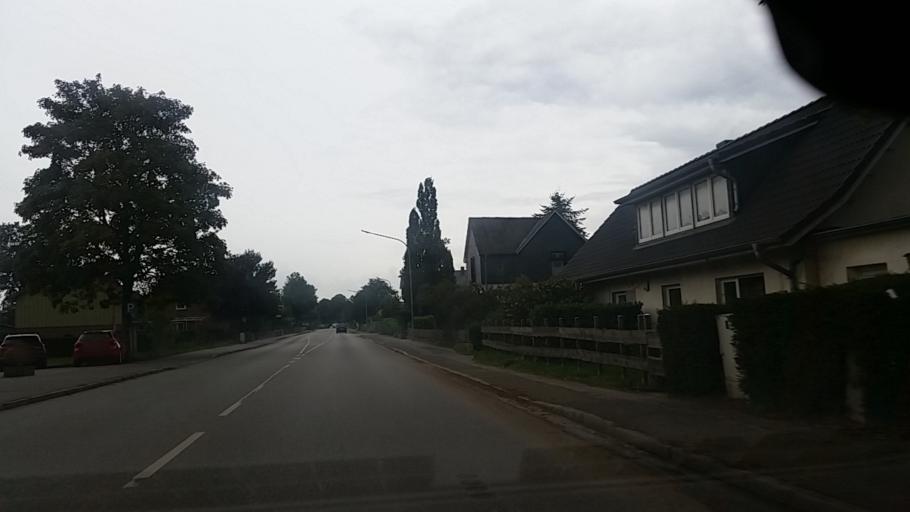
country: DE
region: Schleswig-Holstein
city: Itzstedt
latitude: 53.8061
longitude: 10.1556
